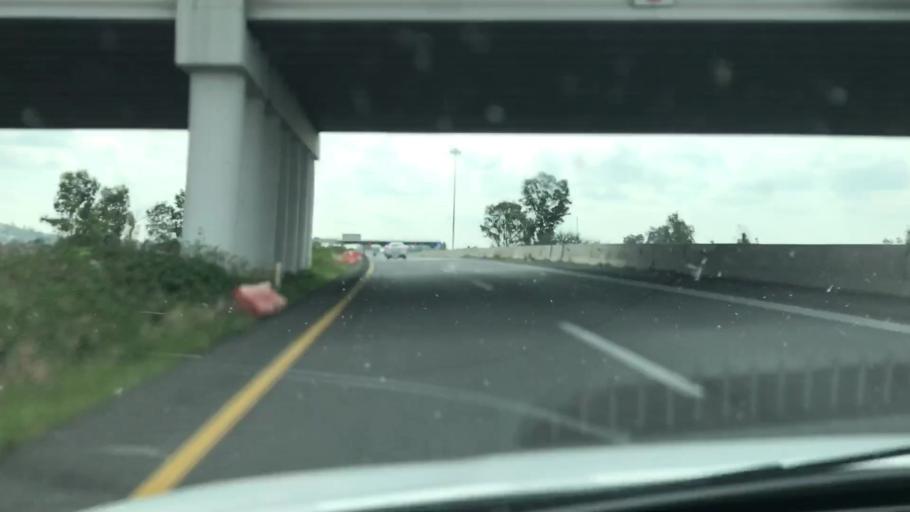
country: MX
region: Guanajuato
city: Cerro Gordo
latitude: 20.5911
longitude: -101.1441
